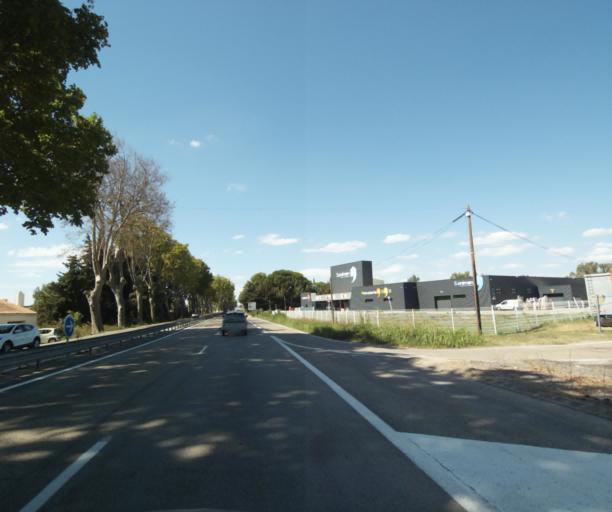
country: FR
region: Languedoc-Roussillon
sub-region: Departement du Gard
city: Rodilhan
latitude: 43.8336
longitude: 4.4217
